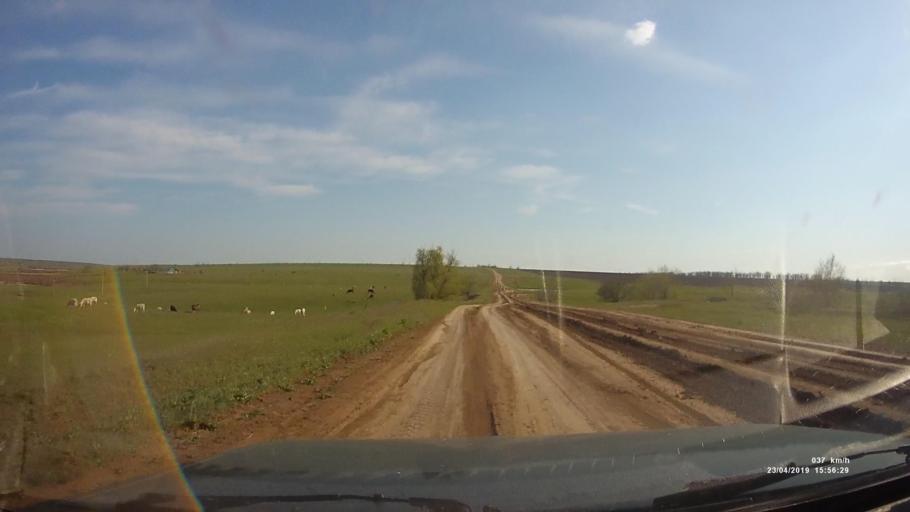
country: RU
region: Rostov
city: Remontnoye
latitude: 46.5368
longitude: 43.1112
